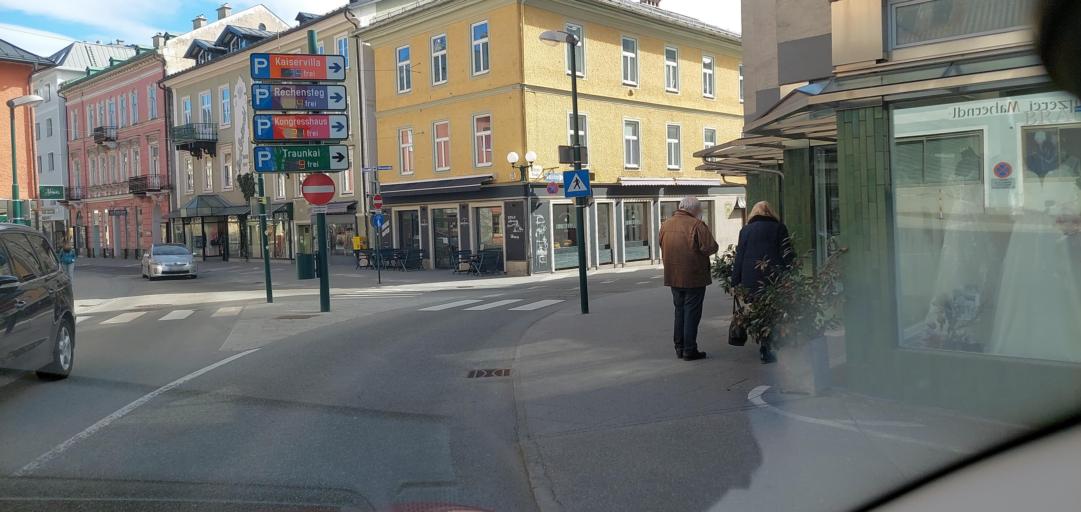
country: AT
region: Upper Austria
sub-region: Politischer Bezirk Gmunden
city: Bad Ischl
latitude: 47.7132
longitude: 13.6201
